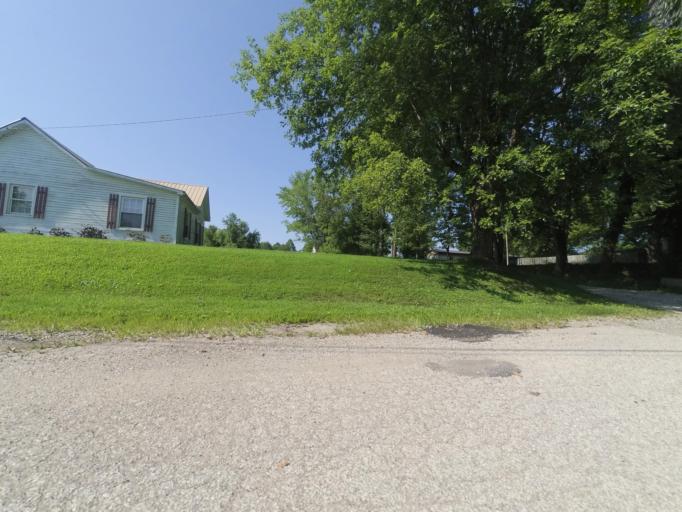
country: US
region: West Virginia
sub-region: Cabell County
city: Huntington
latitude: 38.4363
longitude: -82.4371
